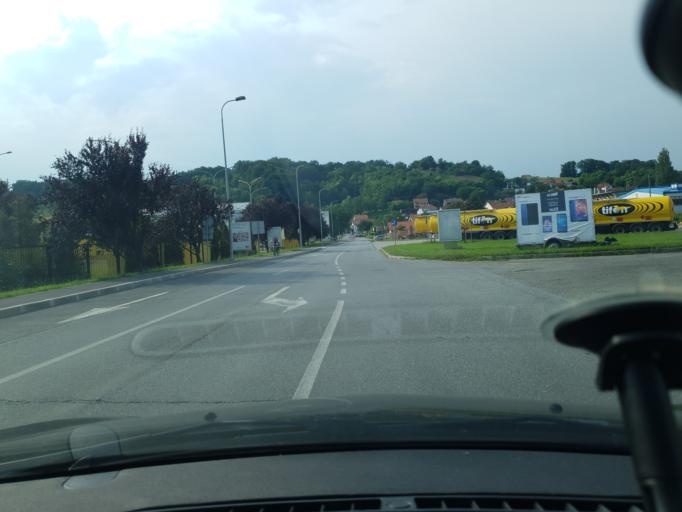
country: HR
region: Krapinsko-Zagorska
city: Zabok
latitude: 46.0207
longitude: 15.9017
